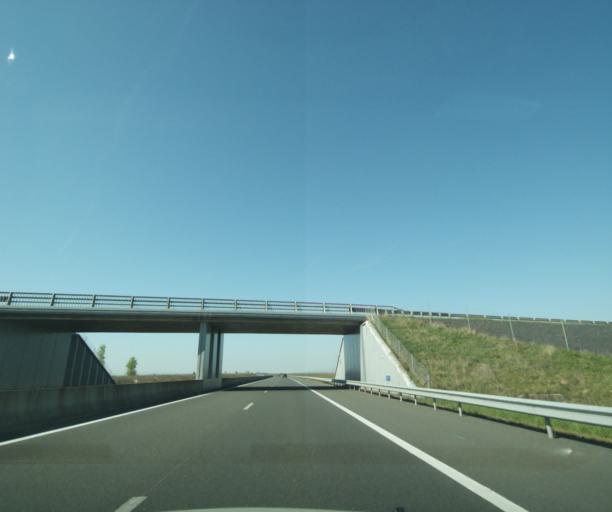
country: FR
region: Centre
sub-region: Departement du Loiret
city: Ascheres-le-Marche
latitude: 48.0764
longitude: 1.9763
